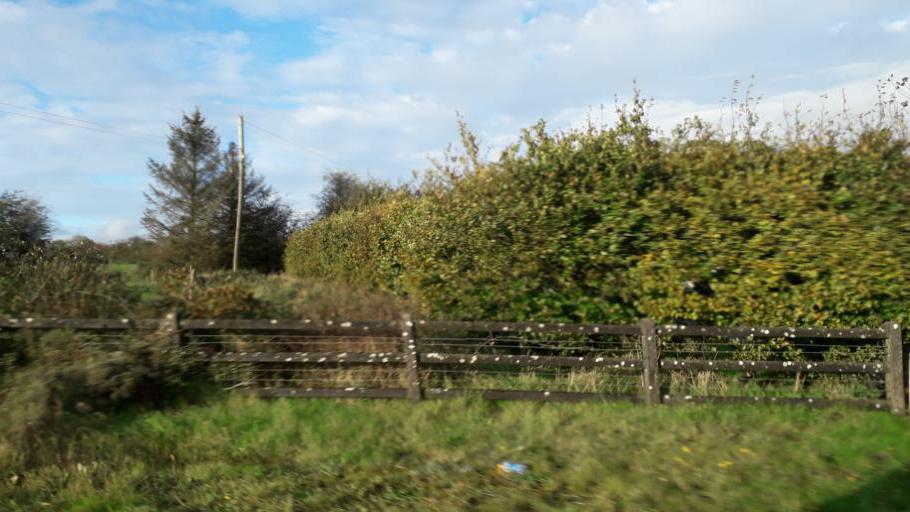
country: IE
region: Connaught
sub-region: Roscommon
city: Roscommon
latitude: 53.7656
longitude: -8.1992
